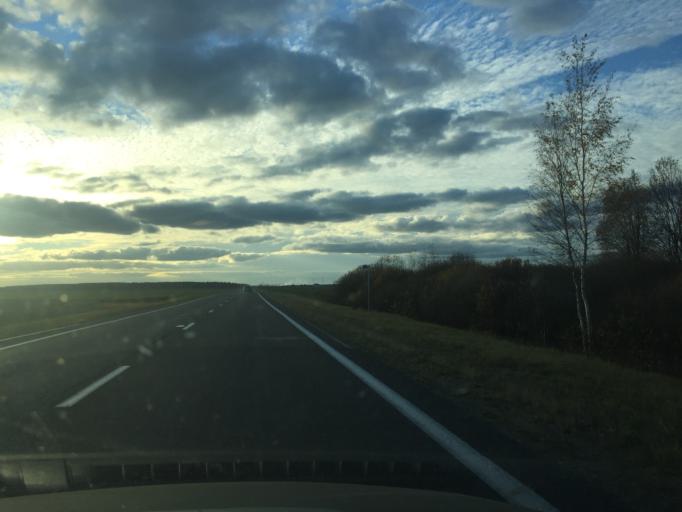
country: BY
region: Vitebsk
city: Vyerkhnyadzvinsk
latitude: 55.8253
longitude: 27.7907
